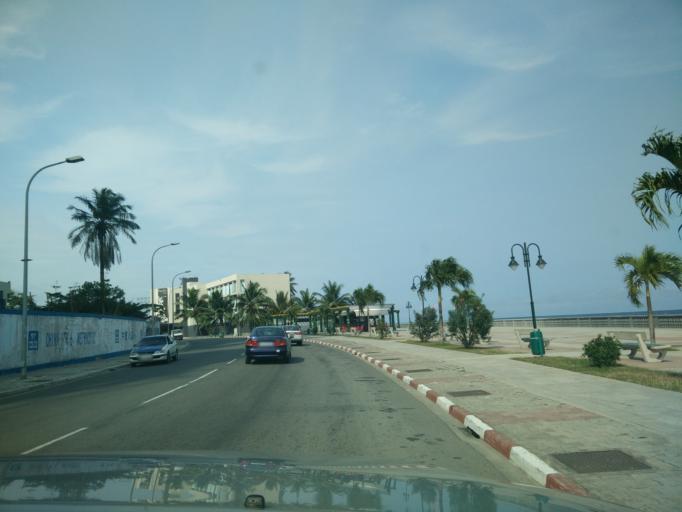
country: GQ
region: Litoral
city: Bata
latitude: 1.8656
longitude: 9.7618
